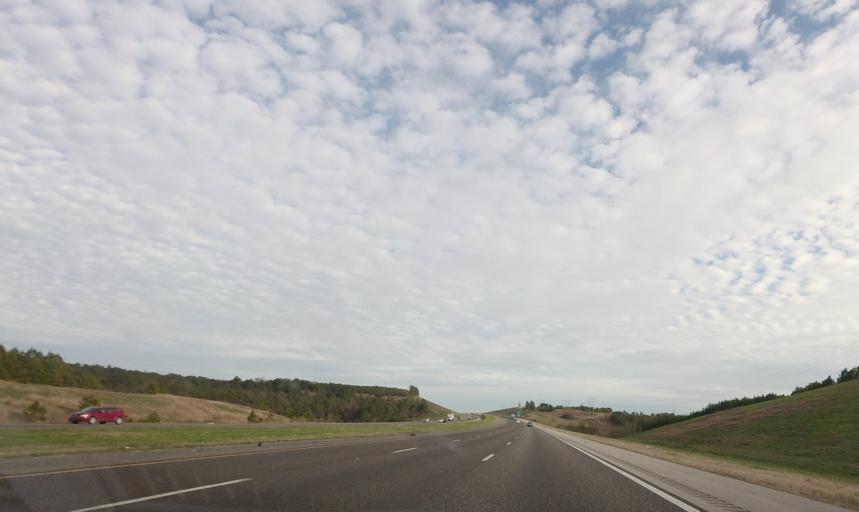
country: US
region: Alabama
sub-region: Jefferson County
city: Graysville
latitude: 33.6517
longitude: -87.0042
